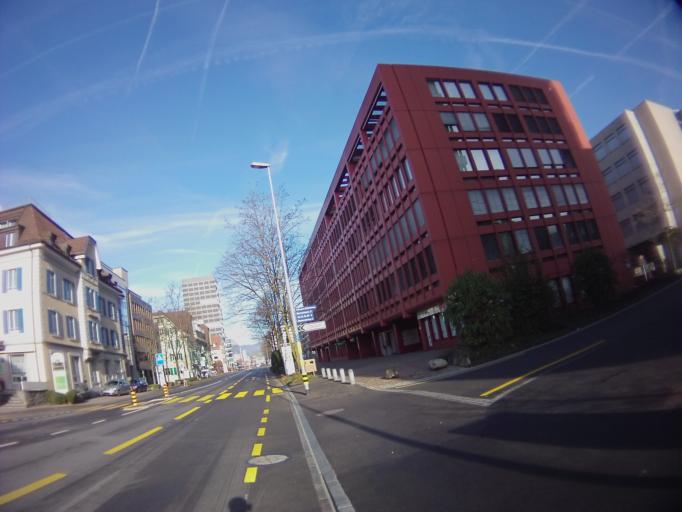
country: CH
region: Zug
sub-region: Zug
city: Zug
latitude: 47.1779
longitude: 8.5184
